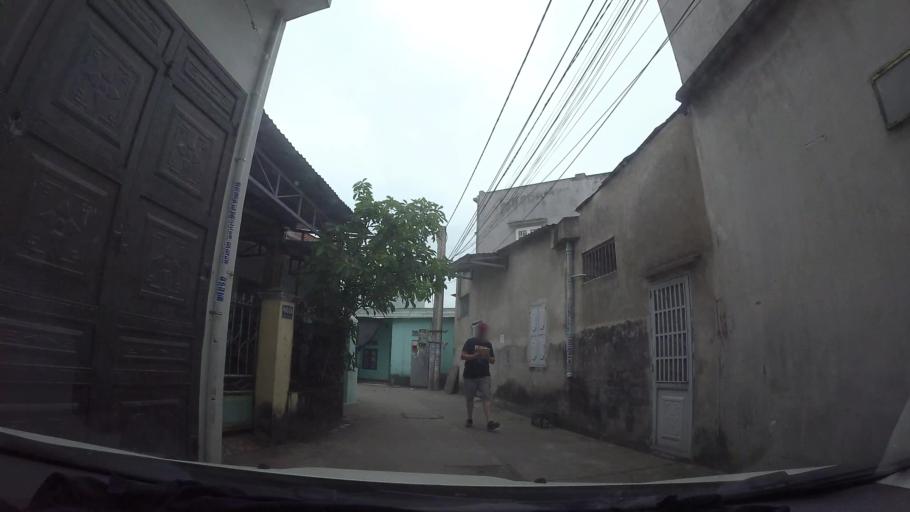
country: VN
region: Da Nang
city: Lien Chieu
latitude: 16.0728
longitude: 108.1438
